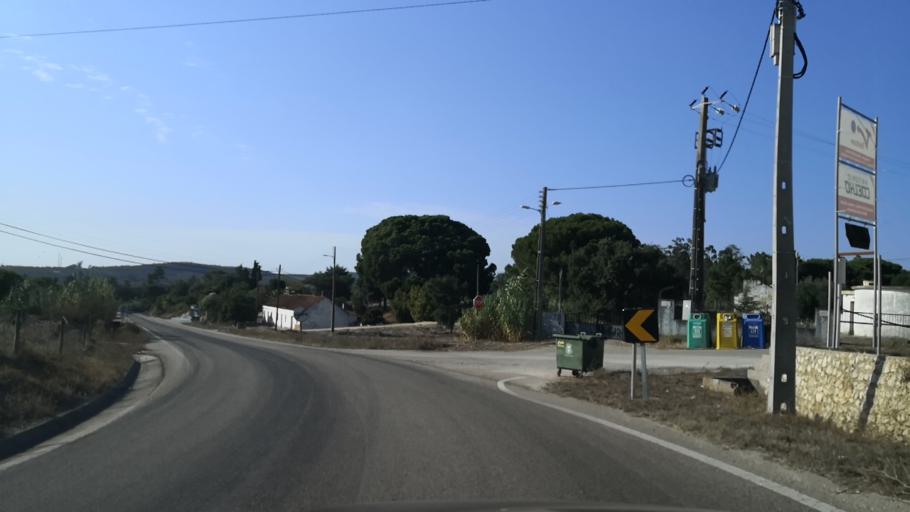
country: PT
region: Santarem
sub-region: Almeirim
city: Fazendas de Almeirim
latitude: 39.1031
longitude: -8.5769
